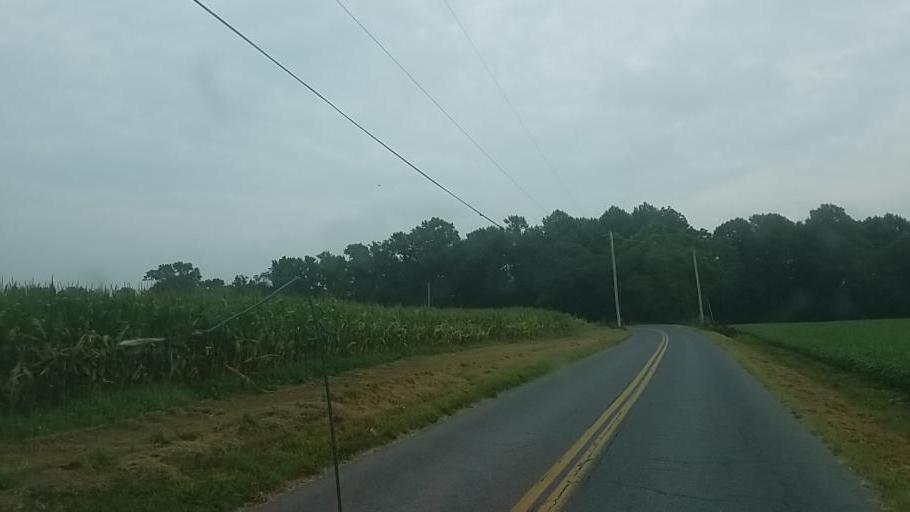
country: US
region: Delaware
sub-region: Sussex County
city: Selbyville
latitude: 38.4380
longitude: -75.1939
